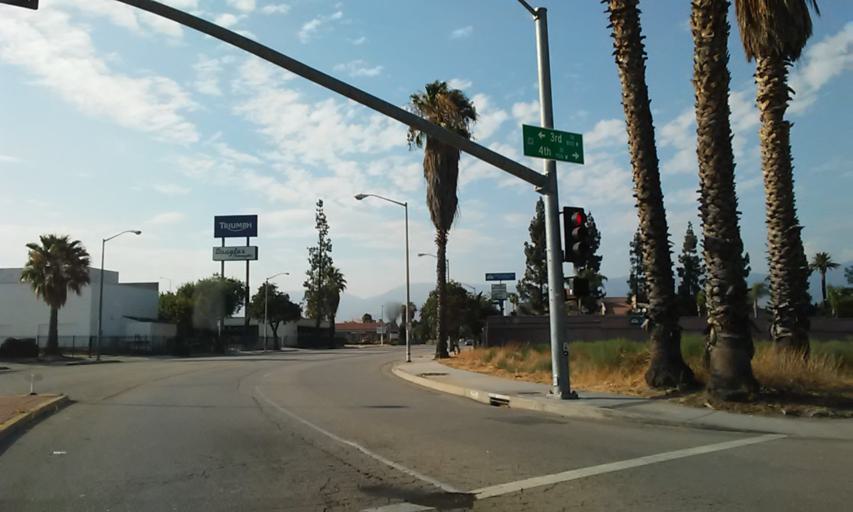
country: US
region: California
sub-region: San Bernardino County
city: San Bernardino
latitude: 34.1051
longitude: -117.3007
